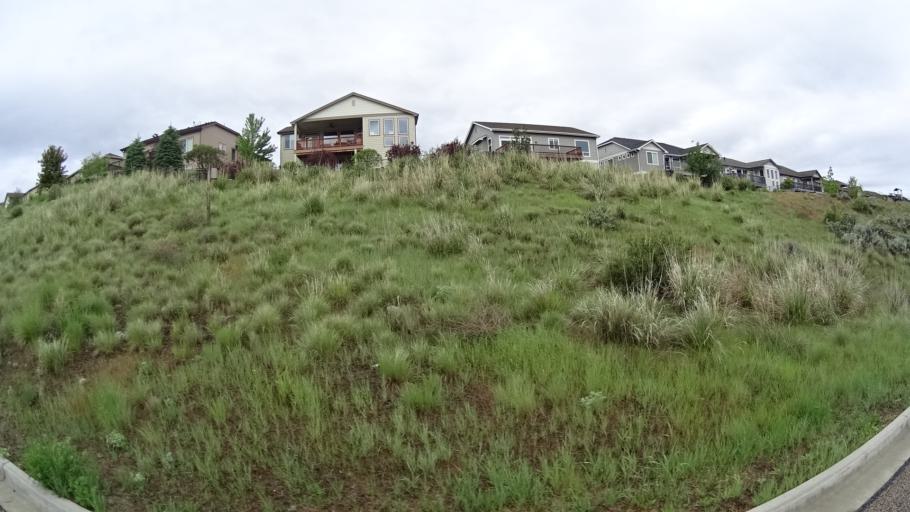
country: US
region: Idaho
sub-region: Ada County
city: Eagle
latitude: 43.7689
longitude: -116.2577
